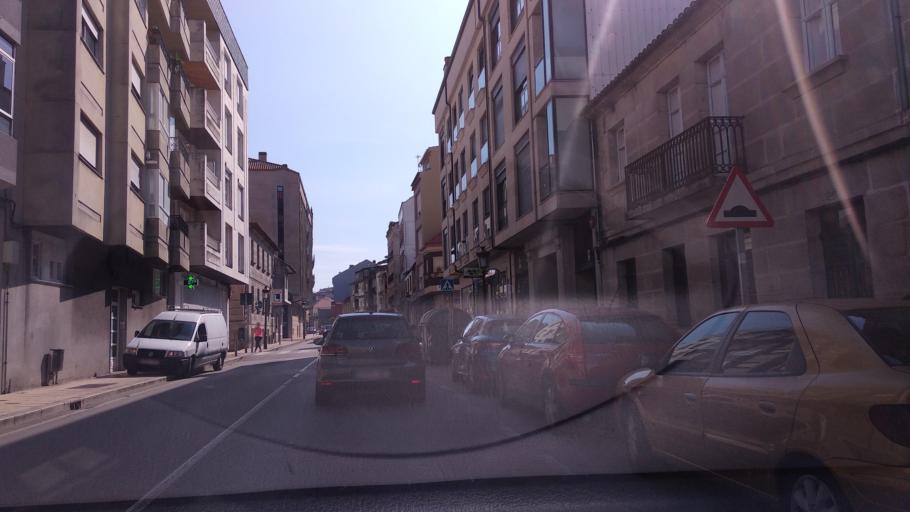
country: ES
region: Galicia
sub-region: Provincia de Pontevedra
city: Moana
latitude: 42.2845
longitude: -8.7349
